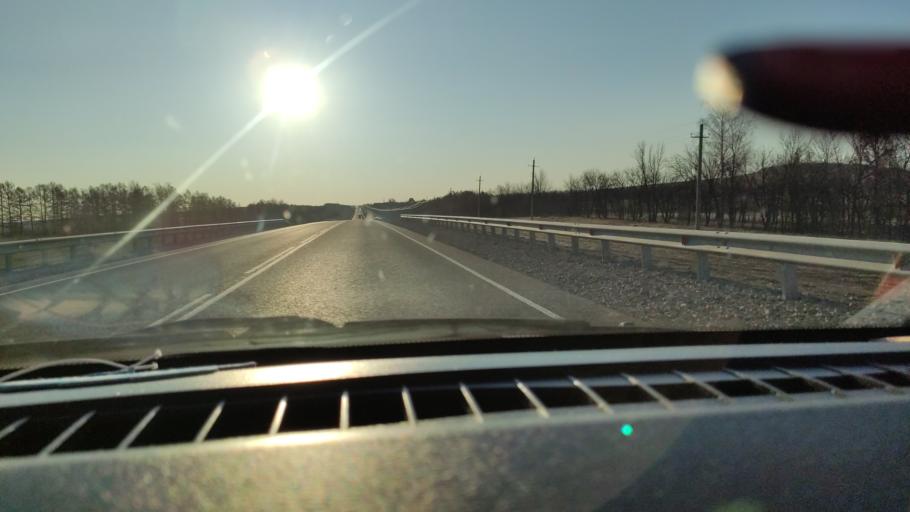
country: RU
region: Saratov
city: Shikhany
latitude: 52.1612
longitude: 47.1285
